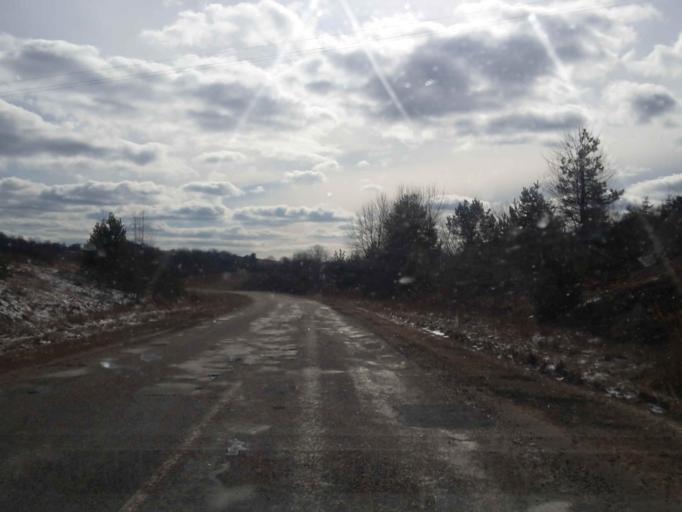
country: BY
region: Vitebsk
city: Mosar
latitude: 55.0798
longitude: 27.2179
